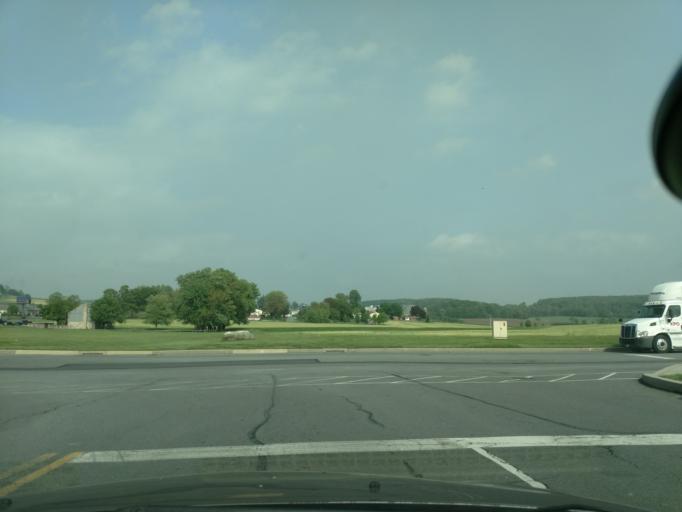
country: US
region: Pennsylvania
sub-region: Chester County
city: Elverson
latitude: 40.1553
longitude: -75.8616
